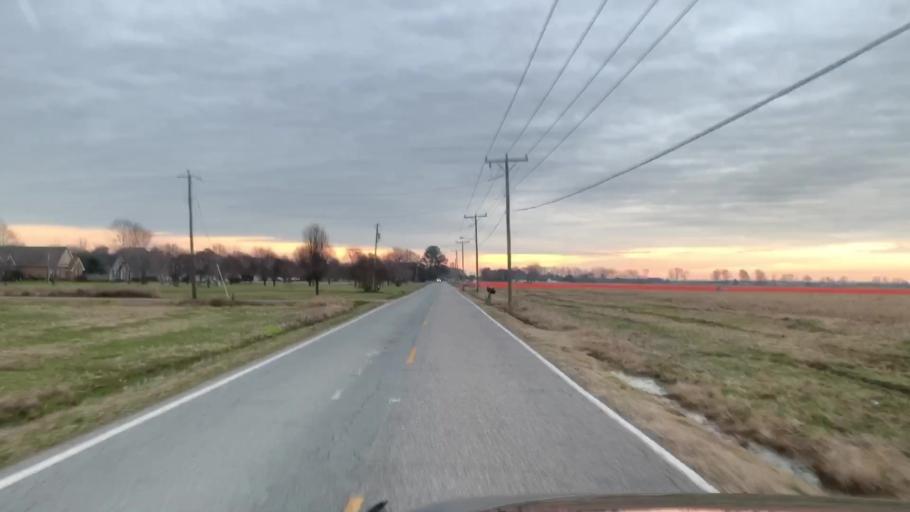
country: US
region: North Carolina
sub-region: Currituck County
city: Moyock
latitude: 36.6299
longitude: -76.1740
